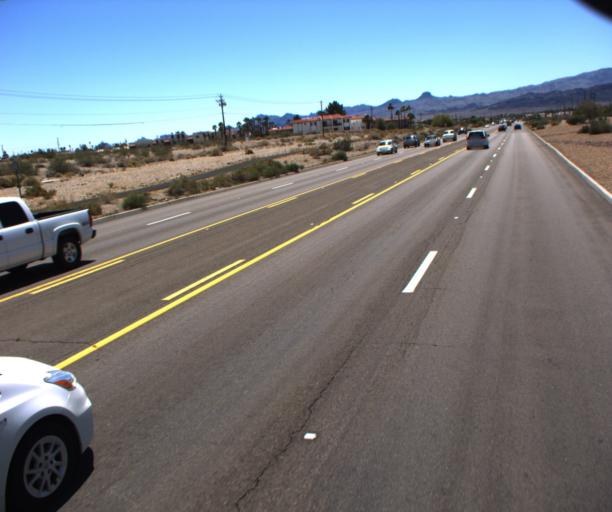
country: US
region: Arizona
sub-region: Mohave County
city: Lake Havasu City
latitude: 34.4874
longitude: -114.3494
